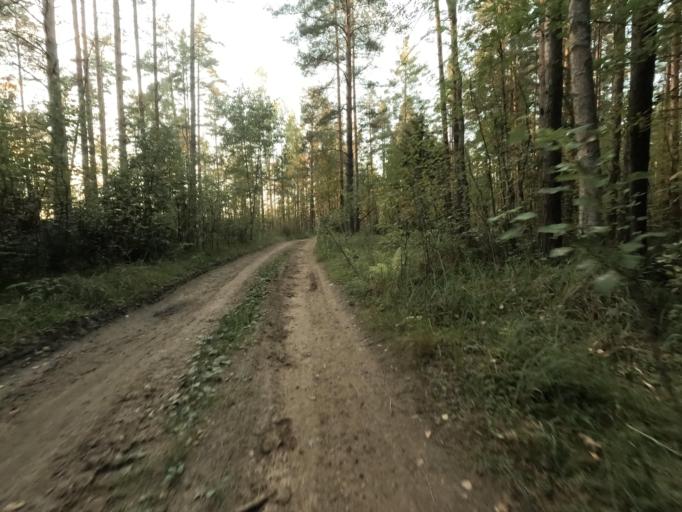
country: RU
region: Leningrad
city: Otradnoye
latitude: 59.8401
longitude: 30.8035
